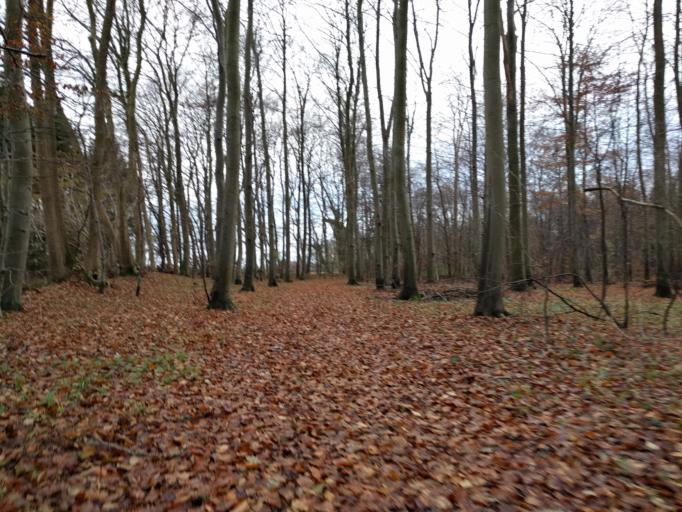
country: DK
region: South Denmark
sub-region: Kerteminde Kommune
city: Langeskov
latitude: 55.4013
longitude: 10.5705
